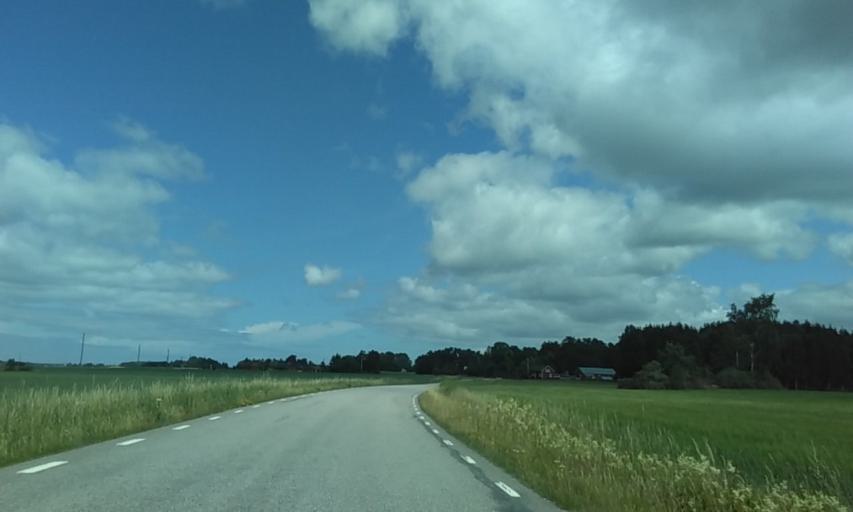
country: SE
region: Vaestra Goetaland
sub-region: Grastorps Kommun
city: Graestorp
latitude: 58.3697
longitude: 12.6867
